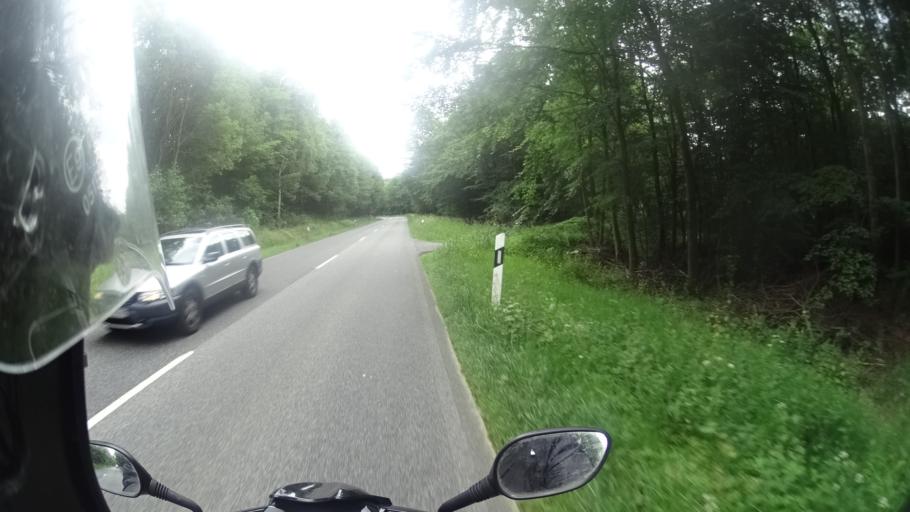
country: DE
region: Hesse
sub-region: Regierungsbezirk Darmstadt
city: Schlangenbad
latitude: 50.0922
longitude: 8.1368
